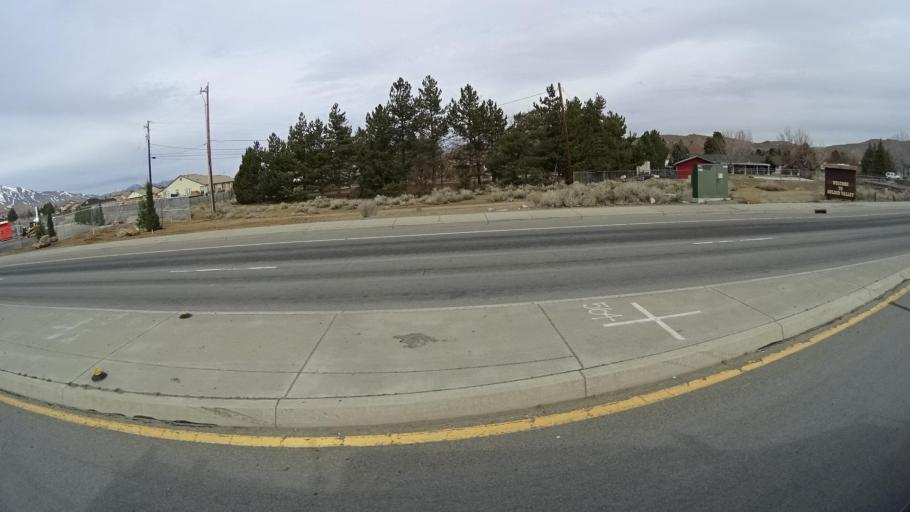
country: US
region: Nevada
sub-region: Washoe County
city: Golden Valley
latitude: 39.6071
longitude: -119.8332
